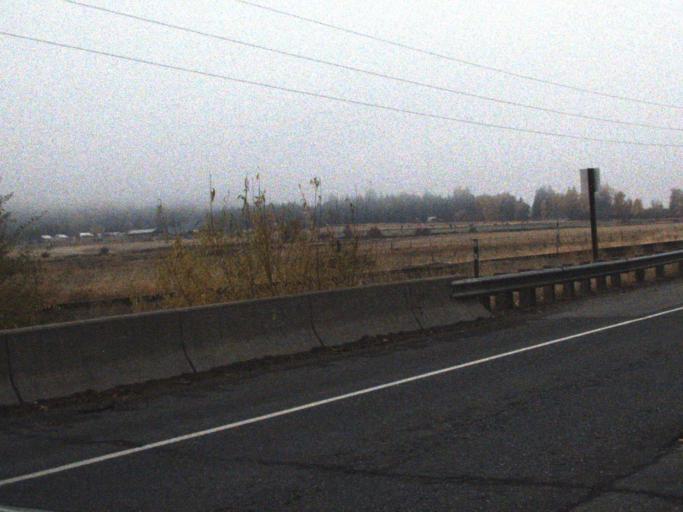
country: US
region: Washington
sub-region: Stevens County
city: Colville
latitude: 48.5731
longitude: -117.9455
